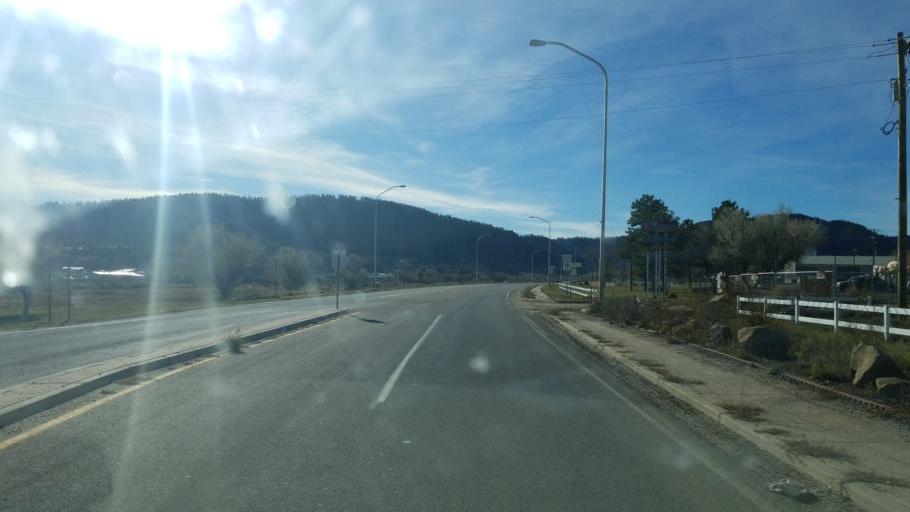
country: US
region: New Mexico
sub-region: Rio Arriba County
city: Dulce
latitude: 36.9338
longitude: -106.9885
